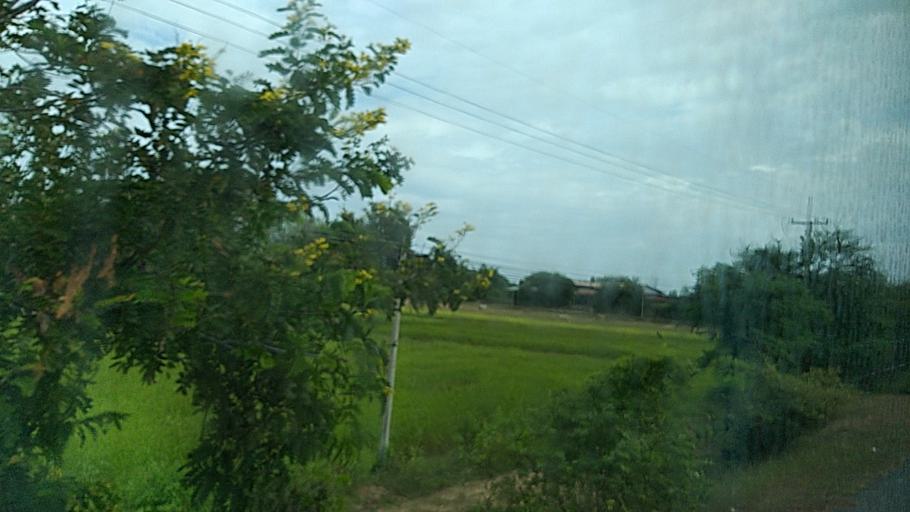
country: TH
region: Kalasin
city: Khong Chai
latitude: 16.1289
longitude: 103.4678
